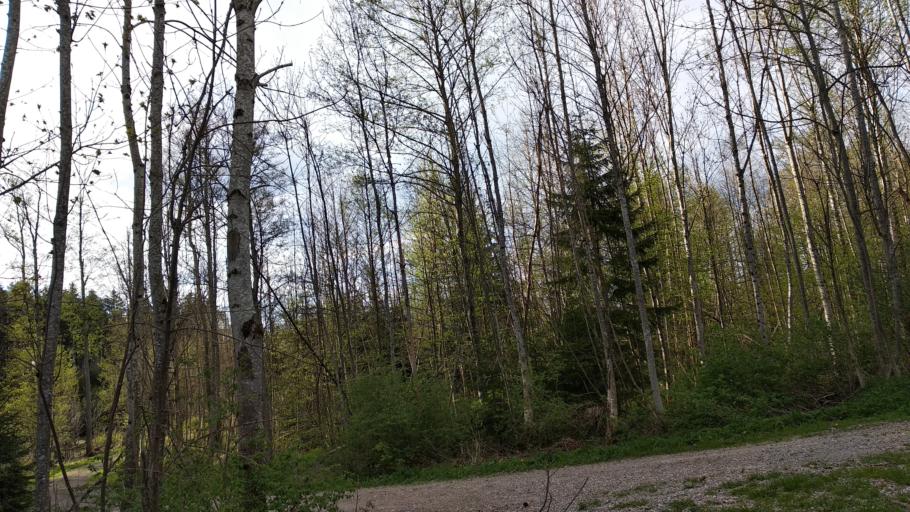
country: DE
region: Bavaria
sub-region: Swabia
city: Woringen
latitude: 47.9312
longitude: 10.1882
